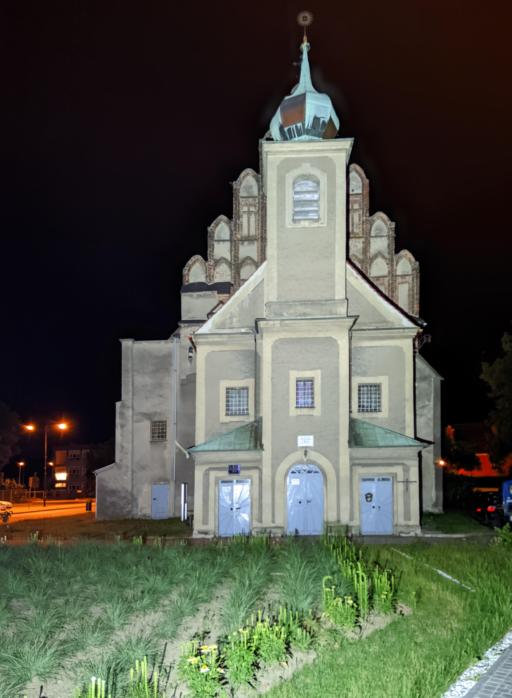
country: PL
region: Opole Voivodeship
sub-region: Powiat nyski
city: Nysa
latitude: 50.4762
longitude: 17.3356
